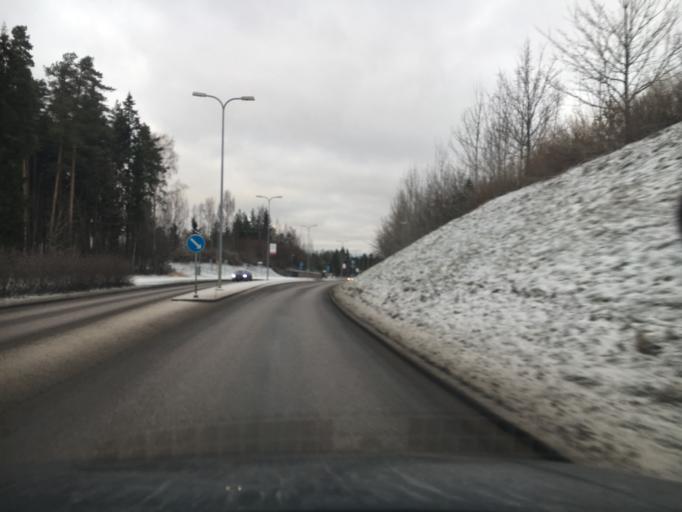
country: FI
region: Uusimaa
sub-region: Helsinki
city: Espoo
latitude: 60.1606
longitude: 24.6590
